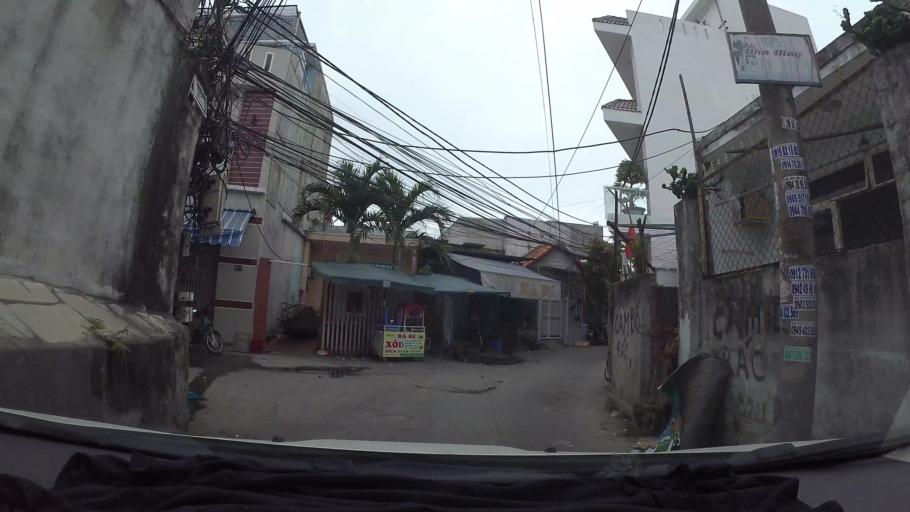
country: VN
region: Da Nang
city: Thanh Khe
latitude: 16.0666
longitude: 108.1781
